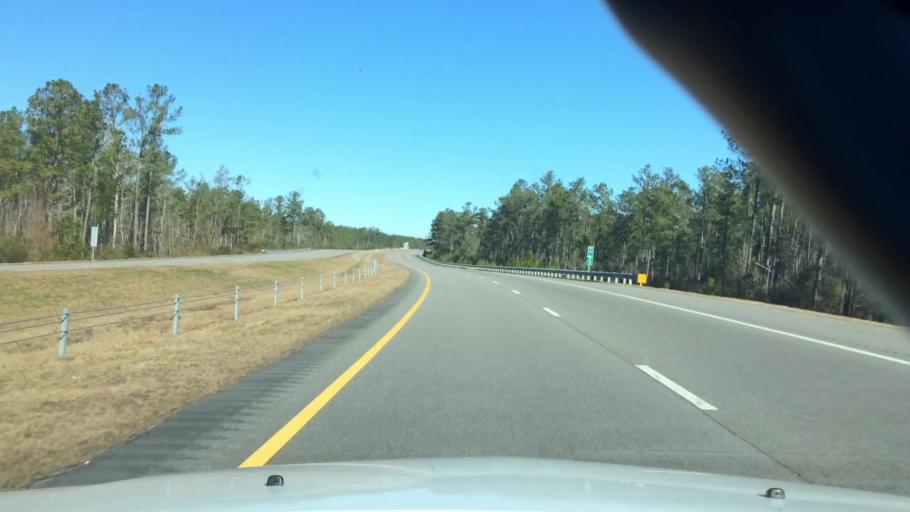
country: US
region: North Carolina
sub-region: Brunswick County
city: Leland
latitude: 34.2114
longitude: -78.0762
